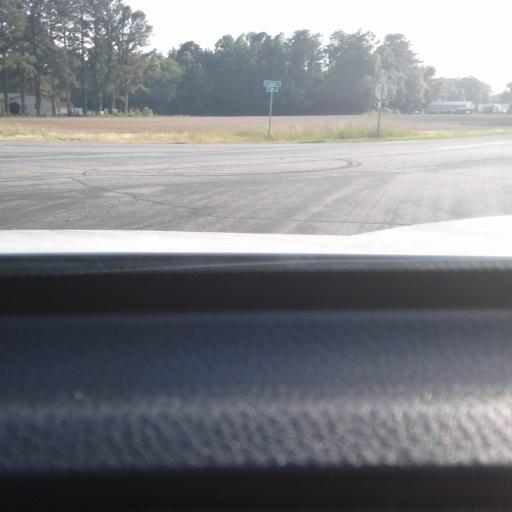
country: US
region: North Carolina
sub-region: Harnett County
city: Dunn
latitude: 35.3347
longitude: -78.5770
